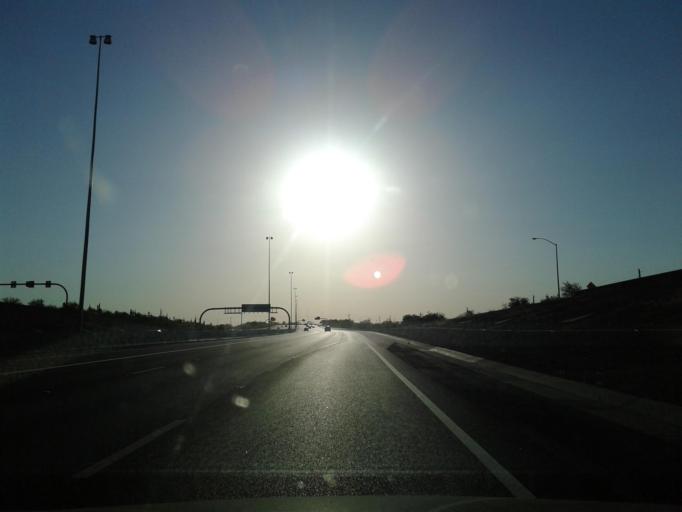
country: US
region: Arizona
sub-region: Maricopa County
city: Mesa
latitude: 33.4809
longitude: -111.7357
